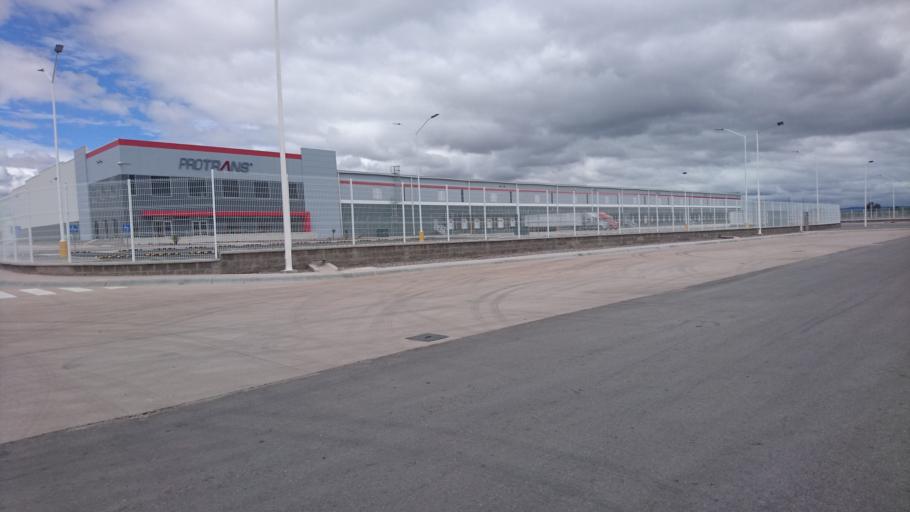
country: MX
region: San Luis Potosi
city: La Pila
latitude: 21.9923
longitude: -100.8594
